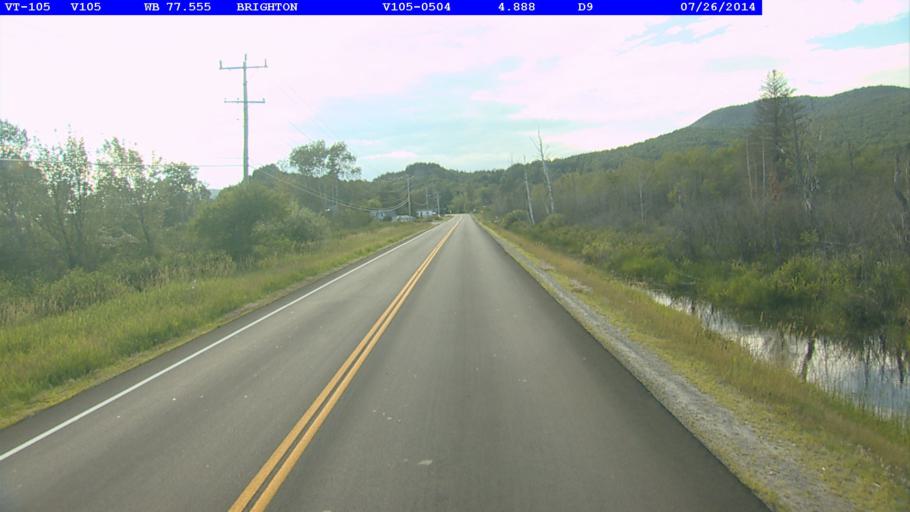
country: US
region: Vermont
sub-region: Caledonia County
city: Lyndonville
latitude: 44.8167
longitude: -71.8720
